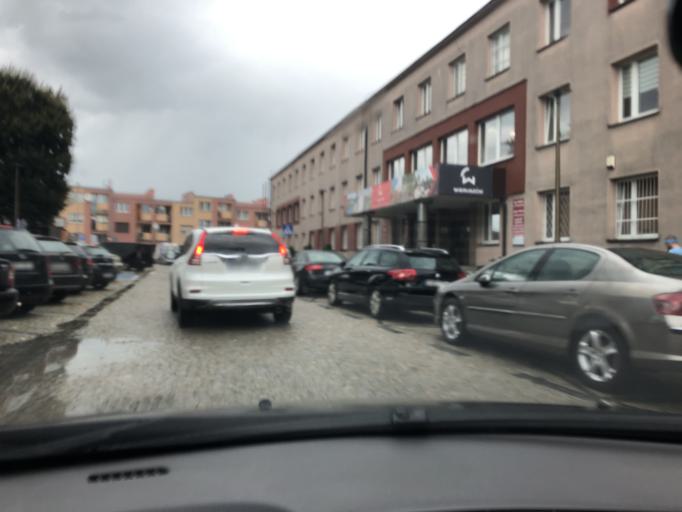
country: PL
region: Lodz Voivodeship
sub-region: Powiat wieruszowski
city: Wieruszow
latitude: 51.2948
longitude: 18.1514
